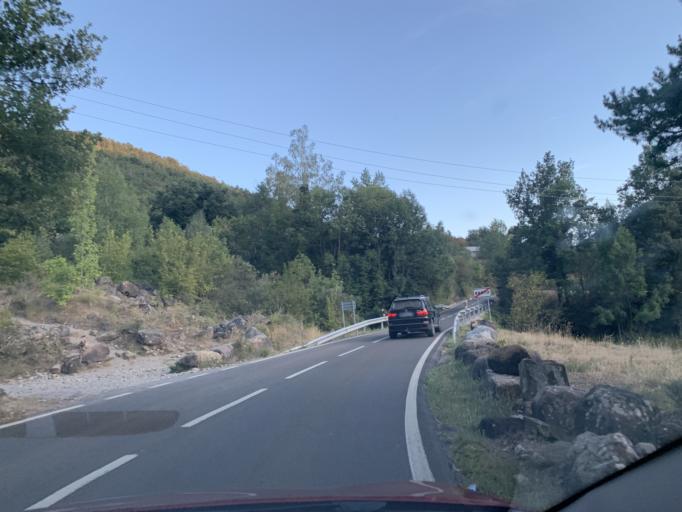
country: ES
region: Aragon
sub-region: Provincia de Huesca
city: Broto
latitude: 42.5983
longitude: -0.1175
